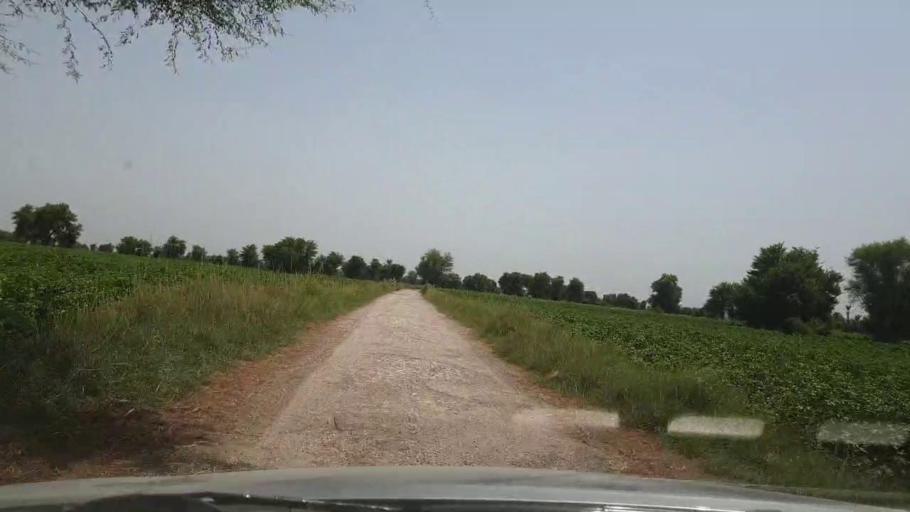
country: PK
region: Sindh
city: Pano Aqil
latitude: 27.7959
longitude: 69.2430
